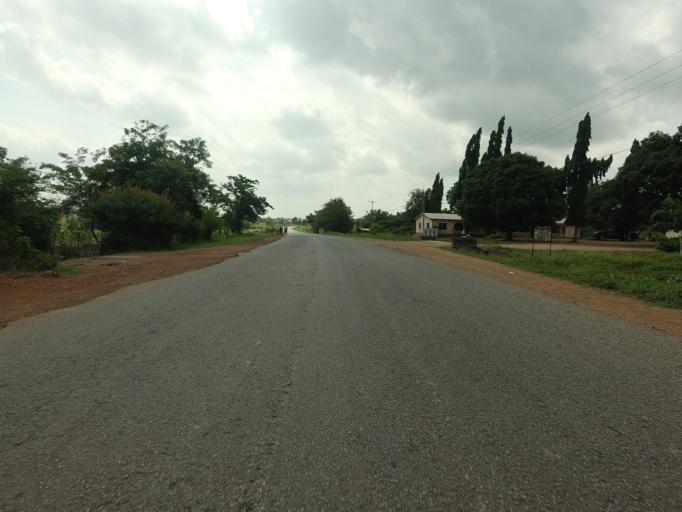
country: GH
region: Volta
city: Ho
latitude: 6.4210
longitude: 0.7378
